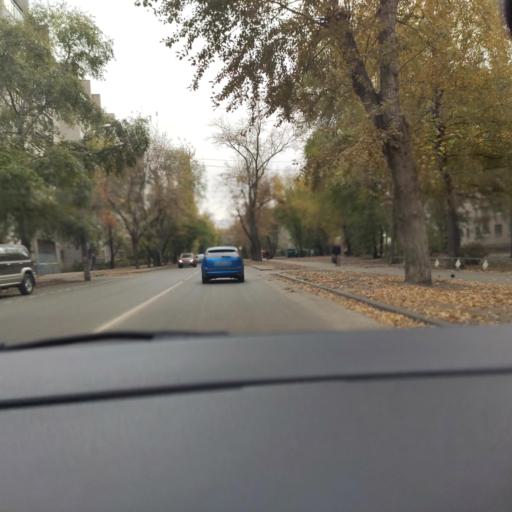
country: RU
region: Voronezj
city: Voronezh
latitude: 51.6852
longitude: 39.1910
